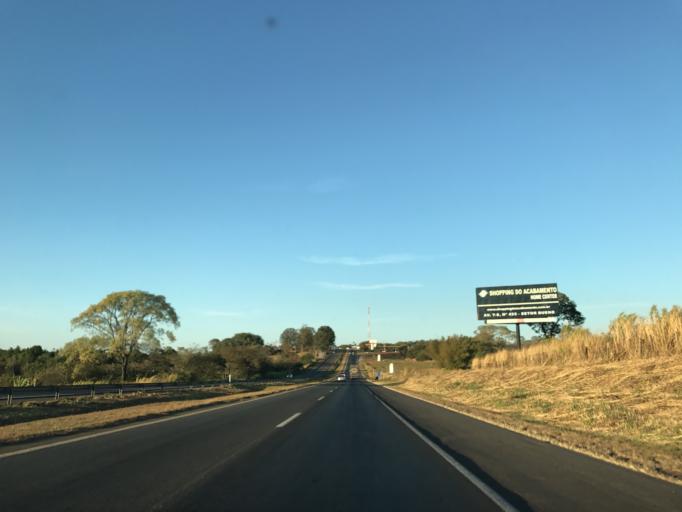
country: BR
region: Goias
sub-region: Goianapolis
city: Goianapolis
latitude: -16.4213
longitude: -49.0125
